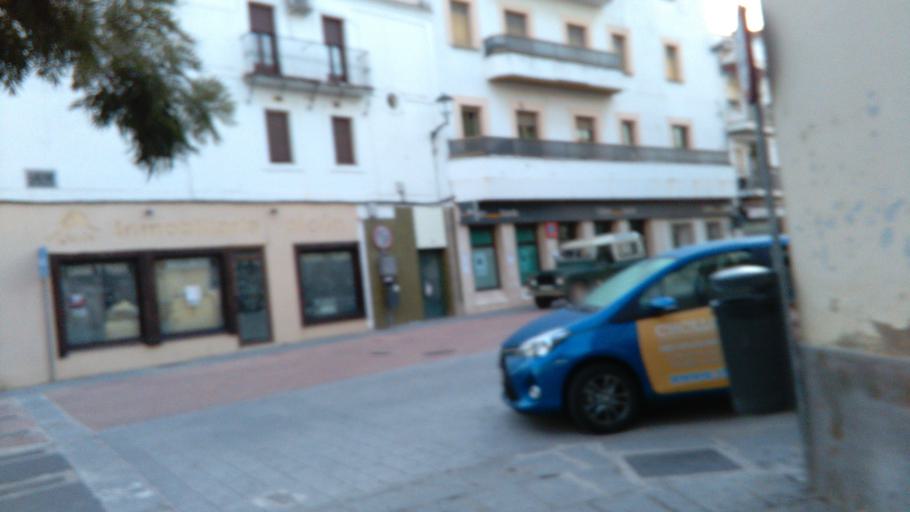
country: ES
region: Extremadura
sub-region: Provincia de Caceres
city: Coria
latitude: 39.9855
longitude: -6.5371
